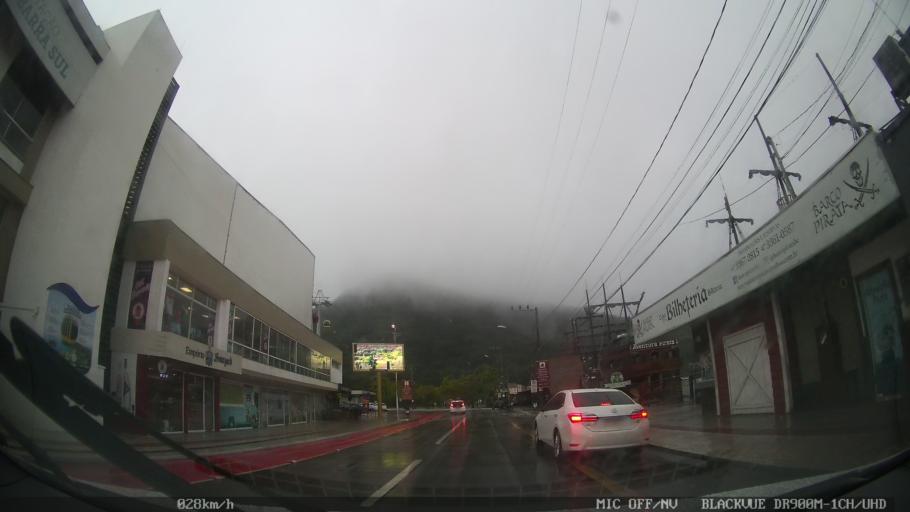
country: BR
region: Santa Catarina
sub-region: Balneario Camboriu
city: Balneario Camboriu
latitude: -27.0055
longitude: -48.6033
